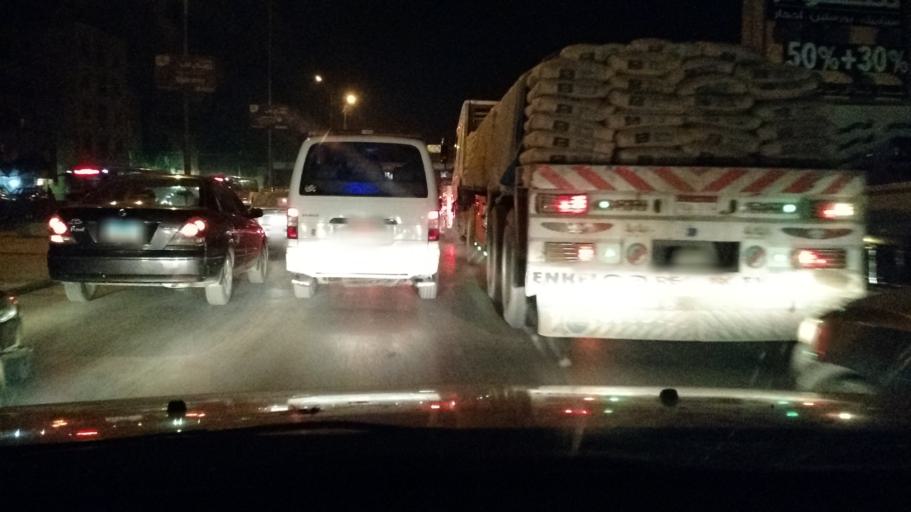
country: EG
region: Al Jizah
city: Al Jizah
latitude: 29.9932
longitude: 31.2822
